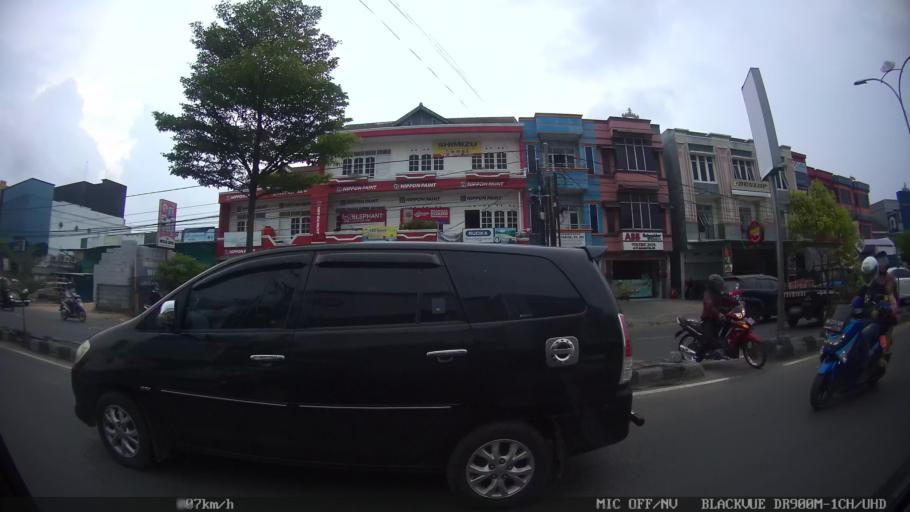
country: ID
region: Lampung
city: Kedaton
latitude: -5.4034
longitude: 105.2807
